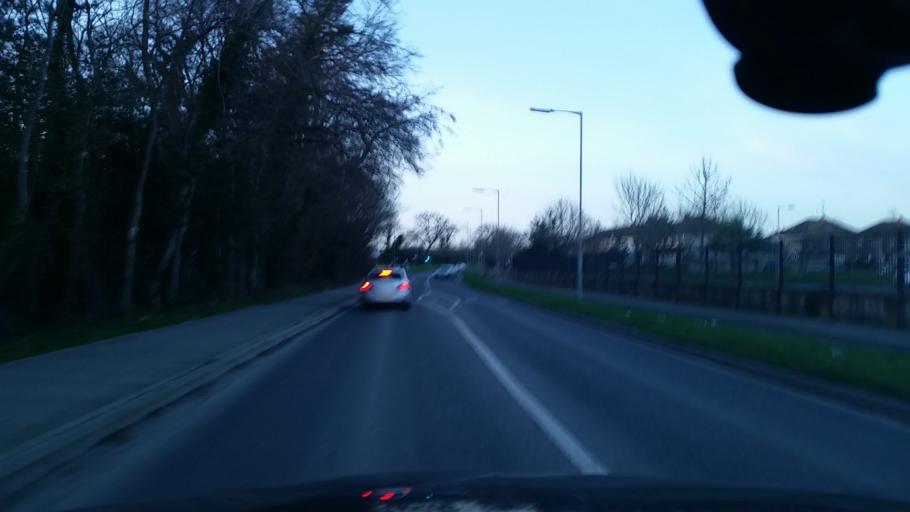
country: IE
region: Leinster
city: Hartstown
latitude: 53.3922
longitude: -6.4316
